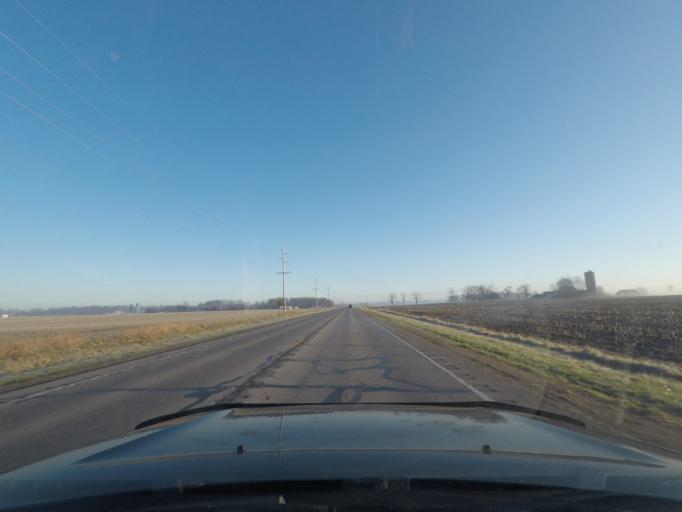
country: US
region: Indiana
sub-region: Elkhart County
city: Wakarusa
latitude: 41.5019
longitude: -86.0020
